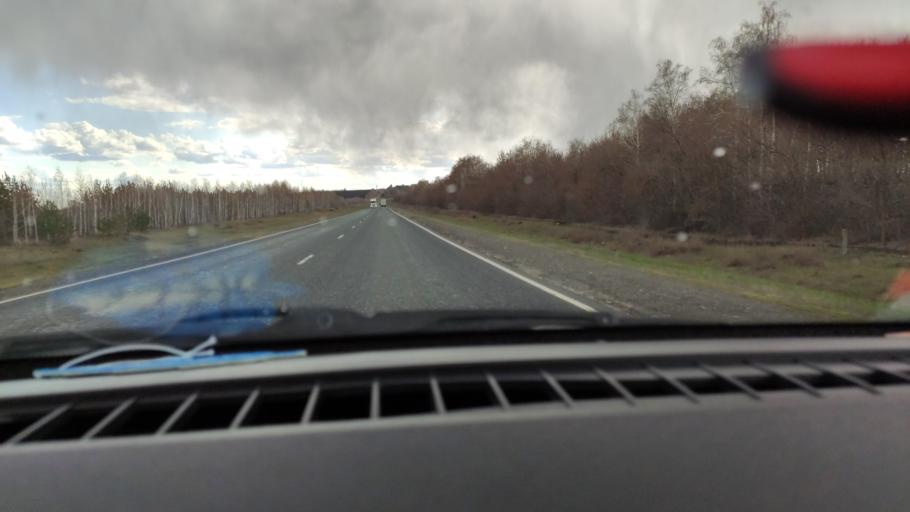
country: RU
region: Saratov
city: Balakovo
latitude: 52.1421
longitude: 47.8023
